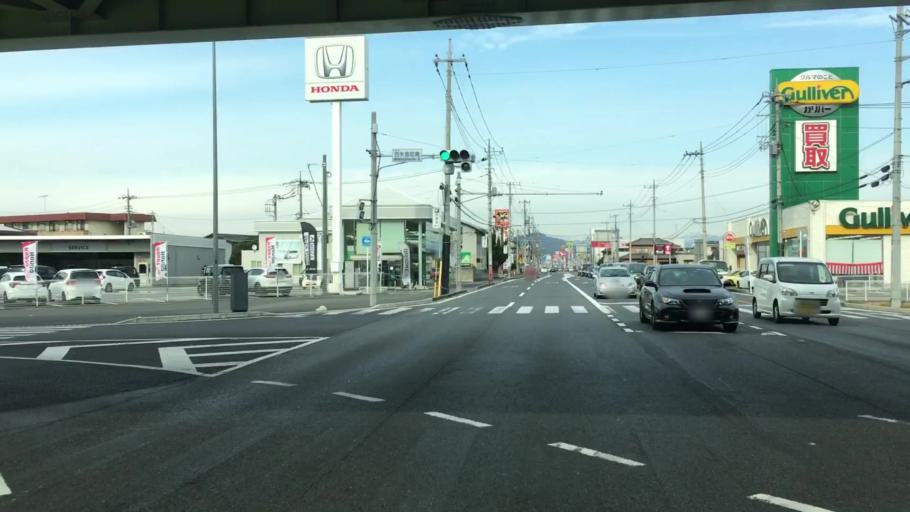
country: JP
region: Gunma
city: Ota
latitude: 36.2693
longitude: 139.3771
